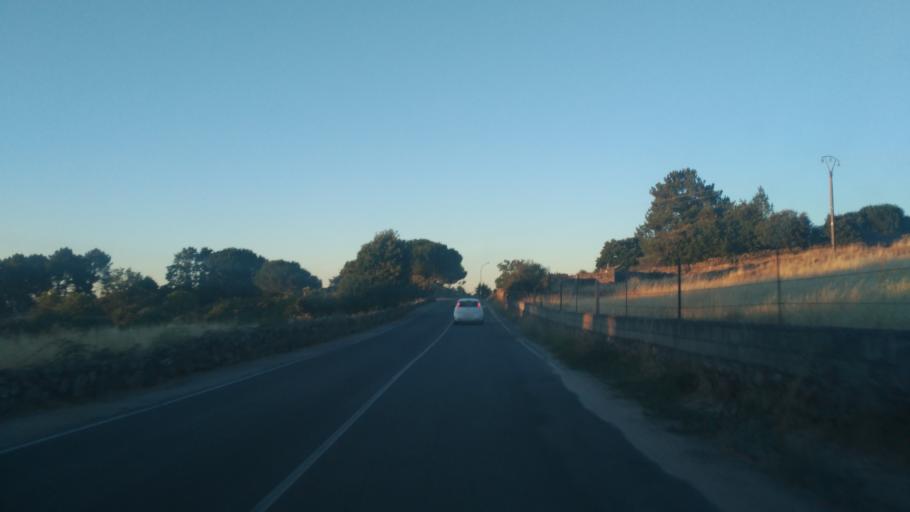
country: ES
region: Castille and Leon
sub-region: Provincia de Salamanca
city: Aldeadavila de la Ribera
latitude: 41.2120
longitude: -6.6196
